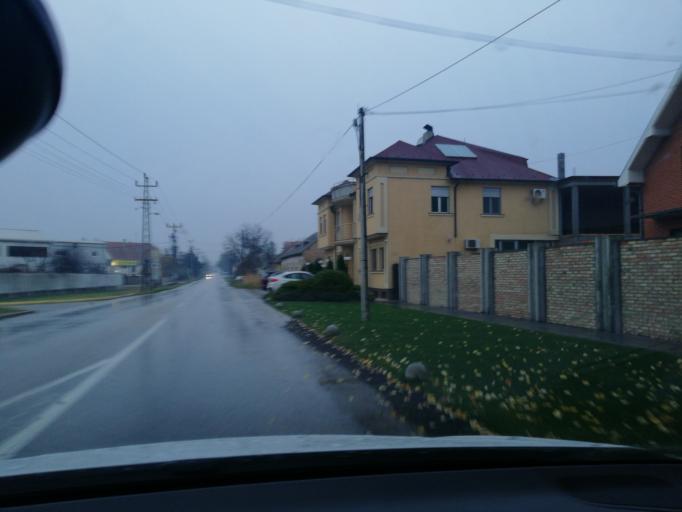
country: RS
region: Autonomna Pokrajina Vojvodina
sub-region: Sremski Okrug
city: Ruma
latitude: 45.0027
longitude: 19.8425
